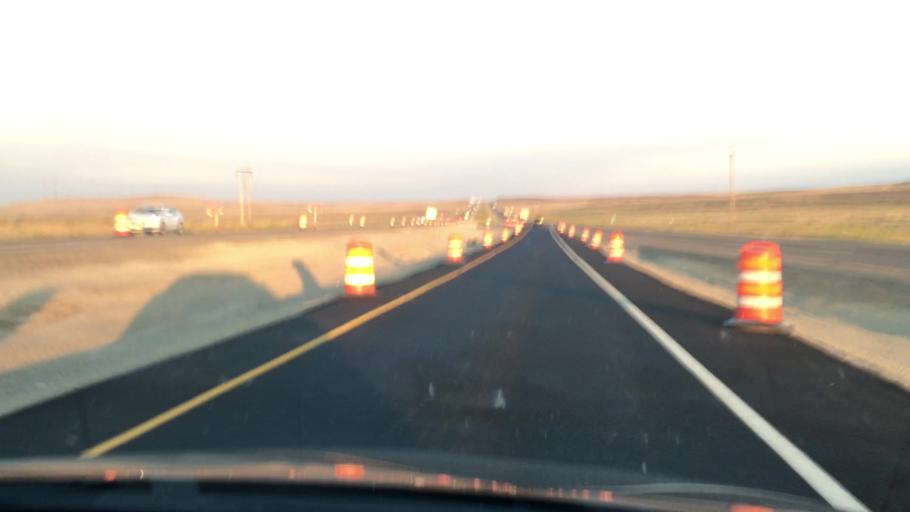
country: US
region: Idaho
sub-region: Minidoka County
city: Rupert
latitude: 42.5609
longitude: -113.5007
